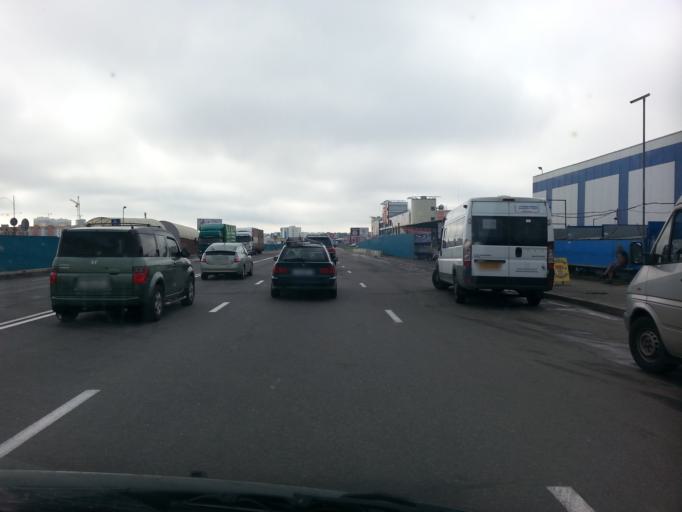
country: BY
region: Minsk
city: Zhdanovichy
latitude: 53.9401
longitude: 27.4415
